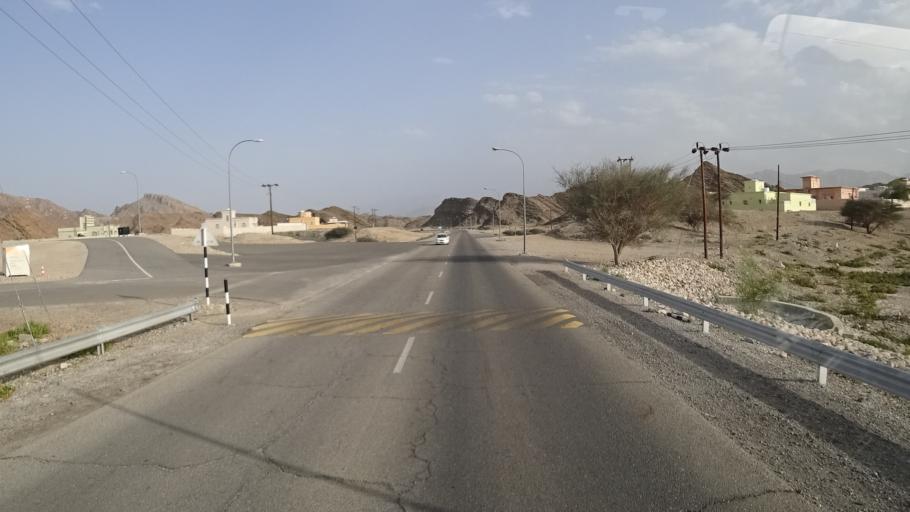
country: OM
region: Muhafazat Masqat
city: Bawshar
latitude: 23.3748
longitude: 58.5163
